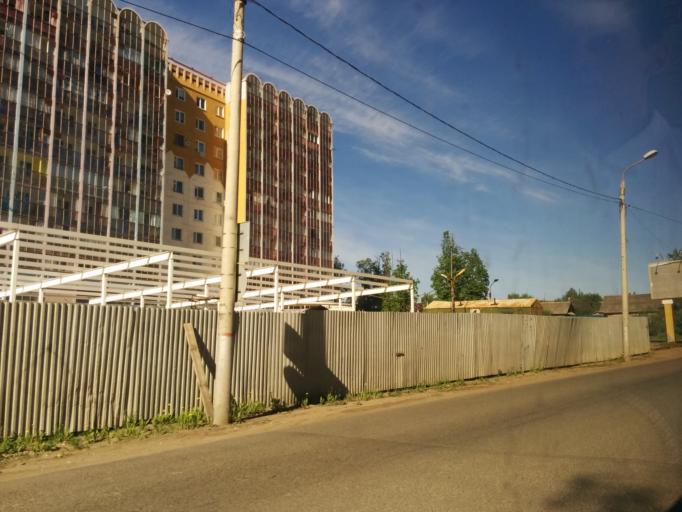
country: RU
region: Perm
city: Kondratovo
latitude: 58.0450
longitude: 56.0830
